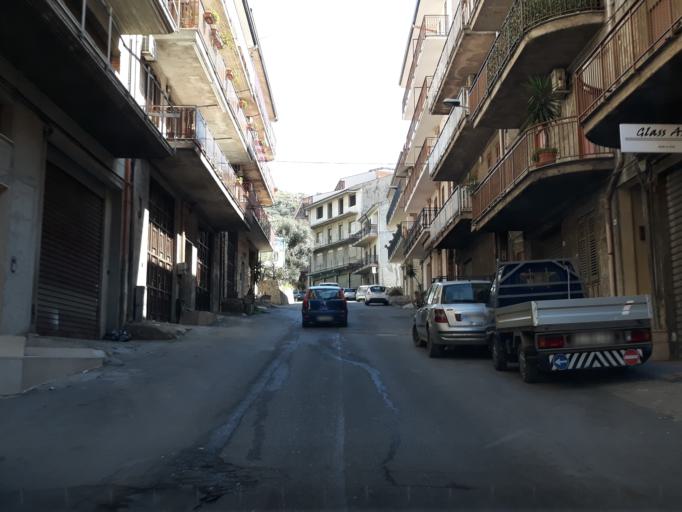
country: IT
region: Sicily
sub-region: Palermo
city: Belmonte Mezzagno
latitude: 38.0463
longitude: 13.3956
